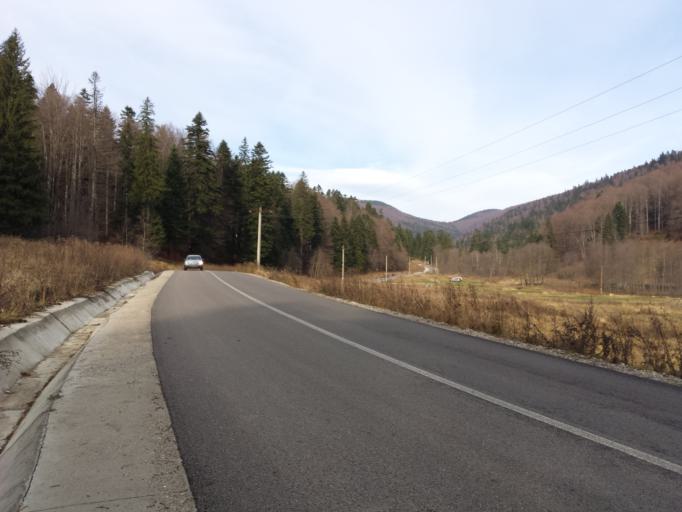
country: RO
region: Prahova
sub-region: Oras Azuga
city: Azuga
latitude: 45.4302
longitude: 25.5323
